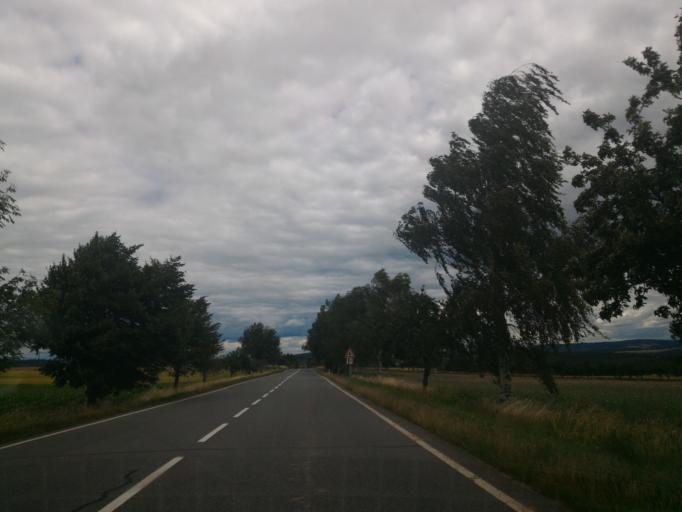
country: CZ
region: Vysocina
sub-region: Okres Pelhrimov
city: Zeliv
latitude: 49.4953
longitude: 15.1794
